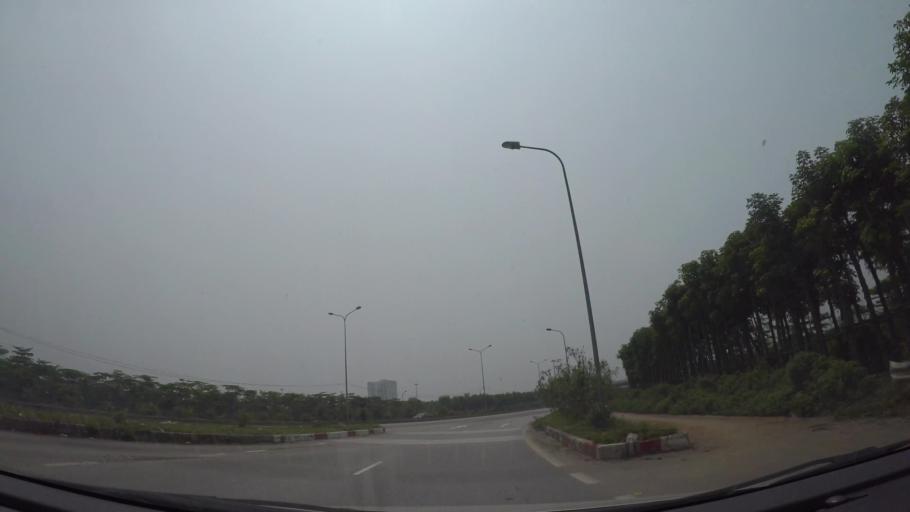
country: VN
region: Ha Noi
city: Lien Quan
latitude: 20.9924
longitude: 105.5240
